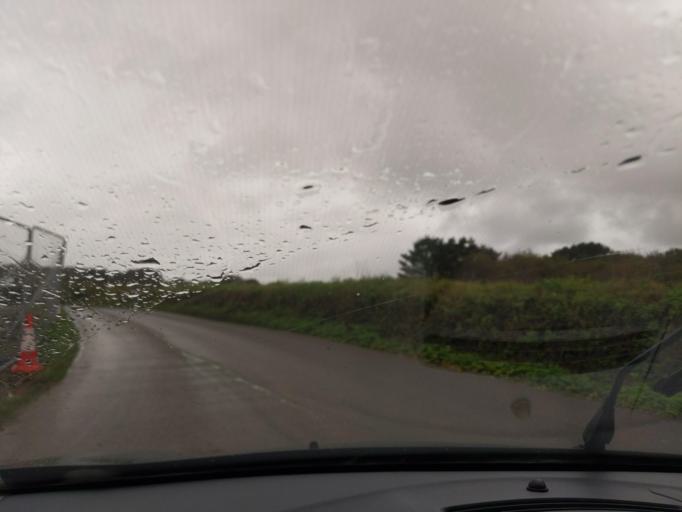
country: GB
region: England
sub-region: Cornwall
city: Wadebridge
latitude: 50.5177
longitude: -4.8199
